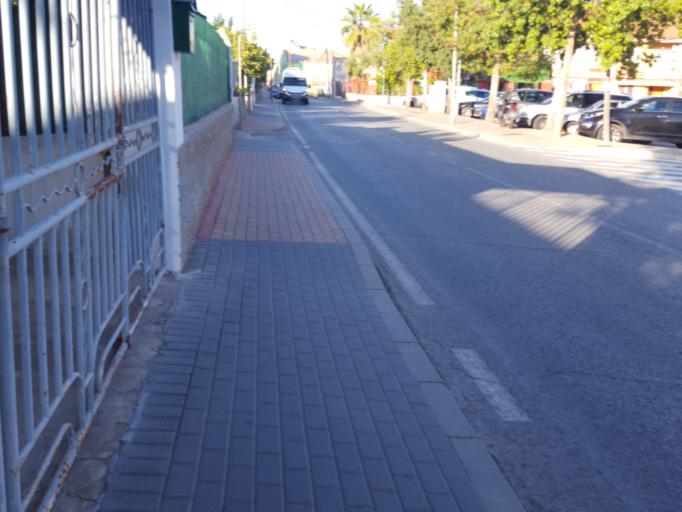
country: ES
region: Murcia
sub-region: Murcia
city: Murcia
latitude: 37.9983
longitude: -1.1736
